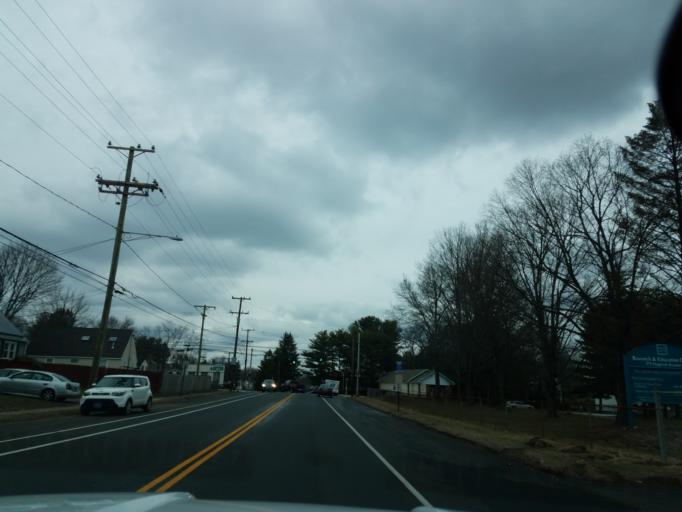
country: US
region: Connecticut
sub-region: Hartford County
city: New Britain
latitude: 41.6833
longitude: -72.8024
